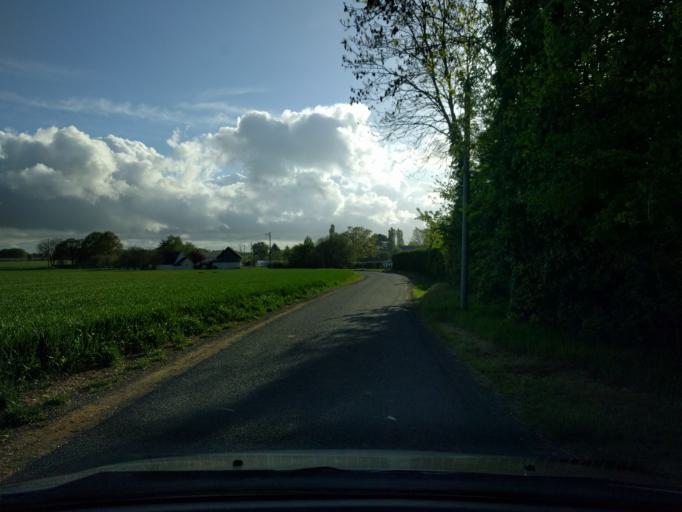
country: FR
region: Haute-Normandie
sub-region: Departement de l'Eure
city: Damville
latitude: 48.8871
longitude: 1.0622
